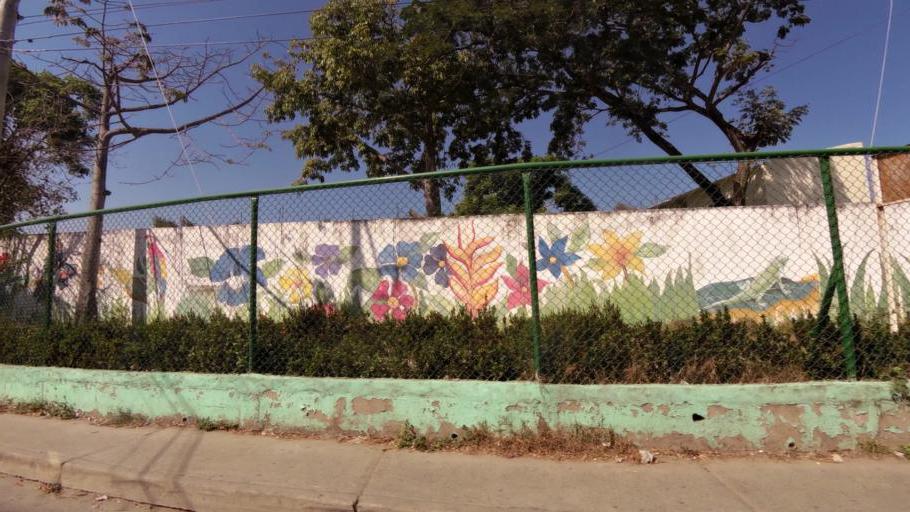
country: CO
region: Bolivar
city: Cartagena
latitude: 10.3935
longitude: -75.5041
